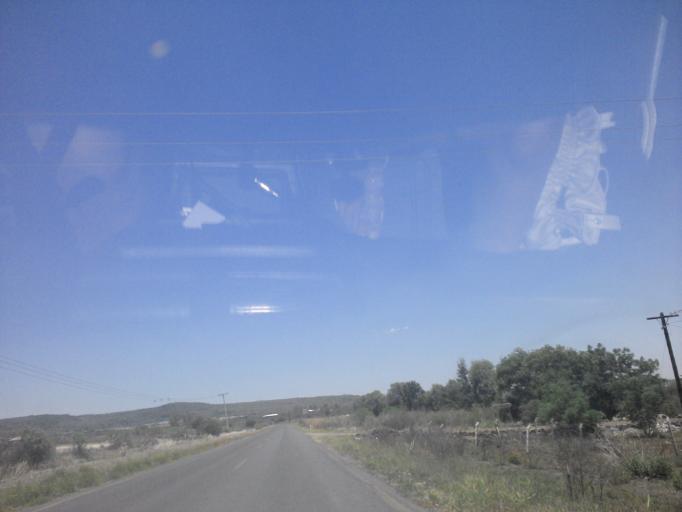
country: MX
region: Guanajuato
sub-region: San Francisco del Rincon
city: San Ignacio de Hidalgo
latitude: 20.8906
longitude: -101.9648
